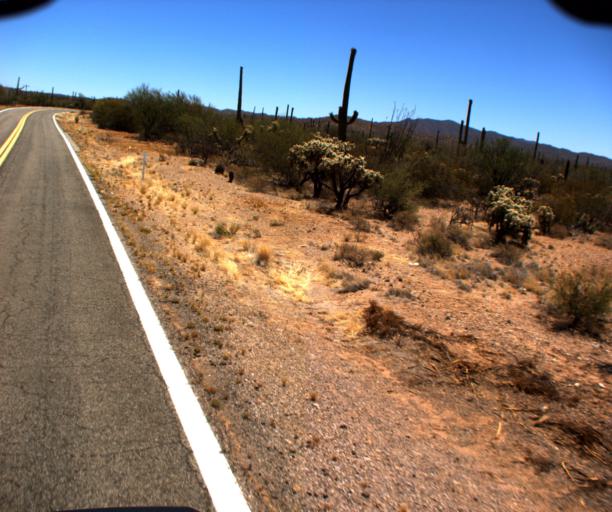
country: US
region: Arizona
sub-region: Pima County
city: Sells
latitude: 32.1764
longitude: -112.2373
